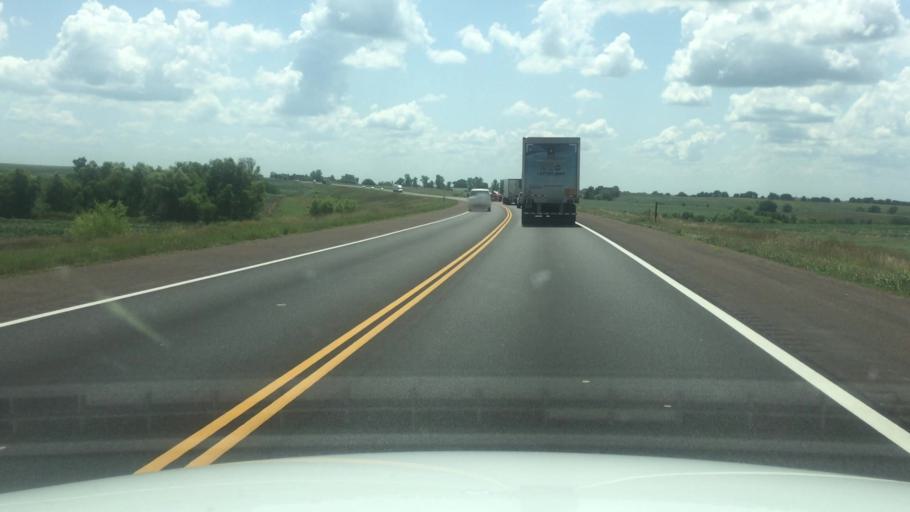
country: US
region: Kansas
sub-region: Nemaha County
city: Sabetha
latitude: 39.8773
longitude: -95.7813
